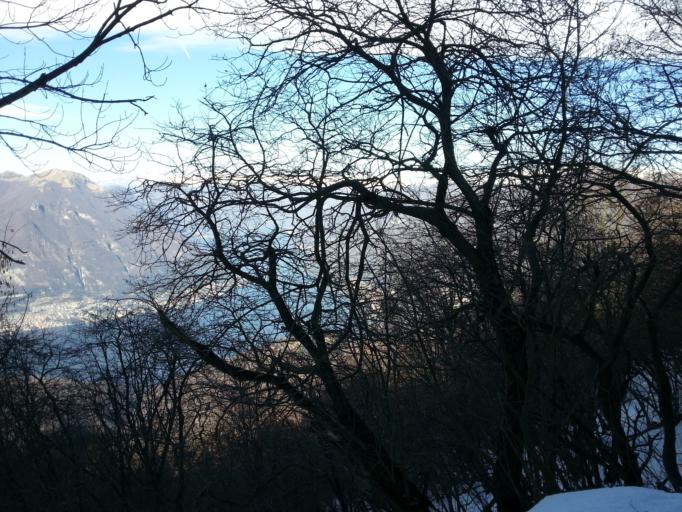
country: IT
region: Lombardy
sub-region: Provincia di Como
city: Lemna
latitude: 45.8368
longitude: 9.1476
